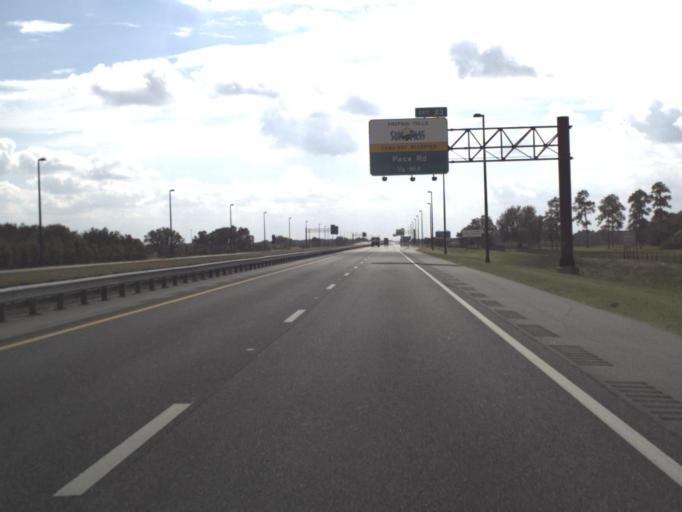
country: US
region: Florida
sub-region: Polk County
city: Polk City
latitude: 28.1473
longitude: -81.8443
